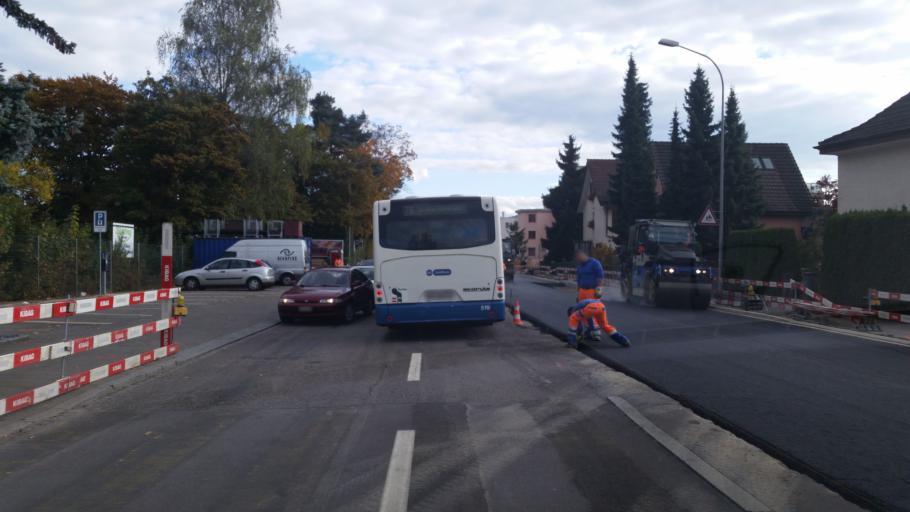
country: CH
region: Zurich
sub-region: Bezirk Zuerich
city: Zuerich (Kreis 11) / Seebach
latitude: 47.4250
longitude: 8.5482
